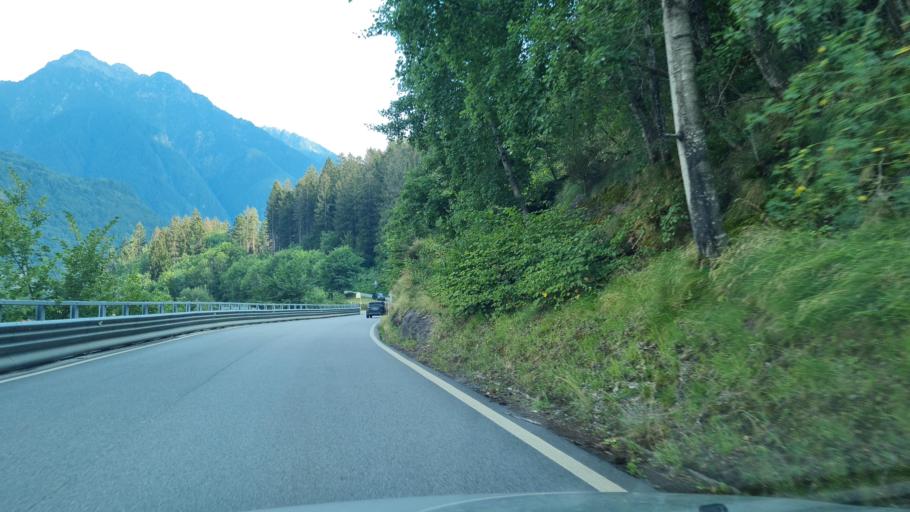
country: IT
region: Piedmont
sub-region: Provincia Verbano-Cusio-Ossola
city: Baceno
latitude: 46.2533
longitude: 8.3202
